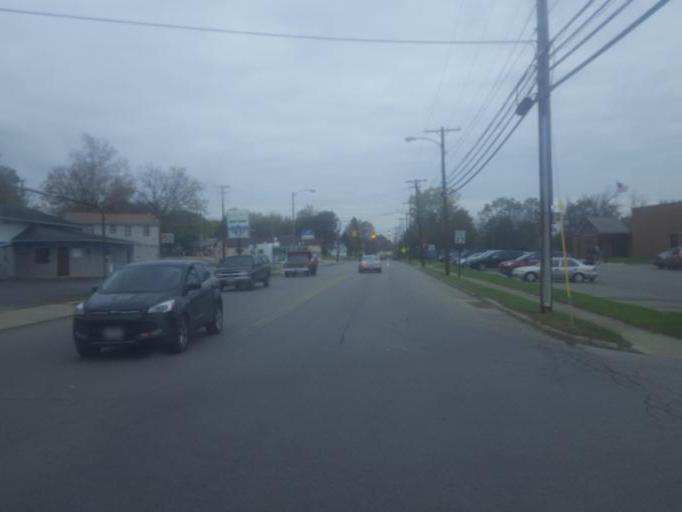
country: US
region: Ohio
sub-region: Richland County
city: Mansfield
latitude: 40.7479
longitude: -82.5082
